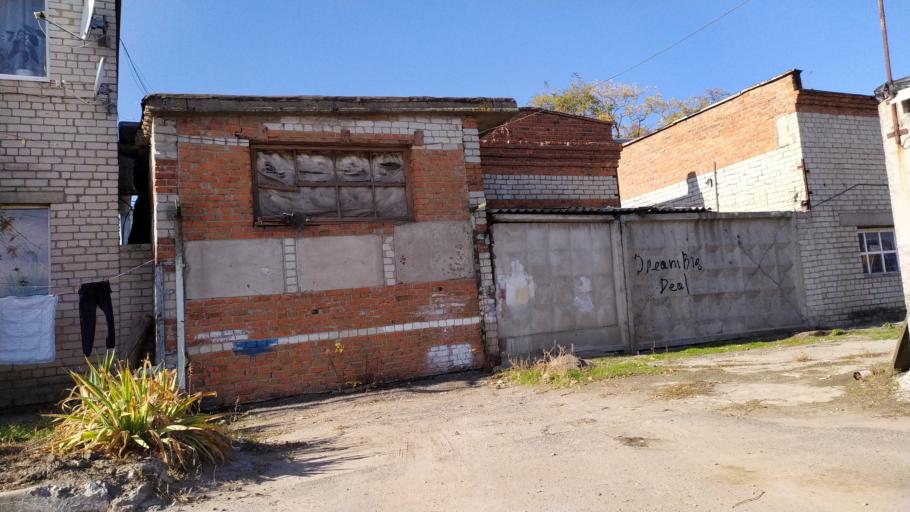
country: RU
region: Kursk
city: Kursk
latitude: 51.6540
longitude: 36.1538
